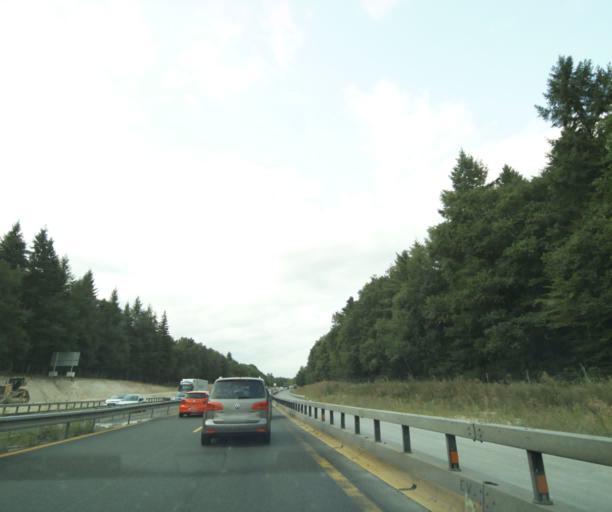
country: FR
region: Centre
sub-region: Departement d'Indre-et-Loire
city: Chambray-les-Tours
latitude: 47.3122
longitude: 0.6896
